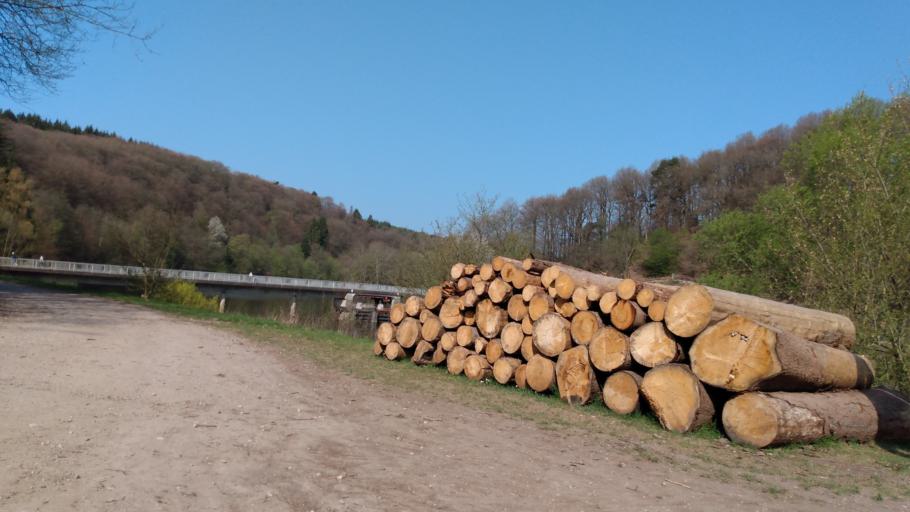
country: DE
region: North Rhine-Westphalia
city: Huckeswagen
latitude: 51.1632
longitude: 7.3300
